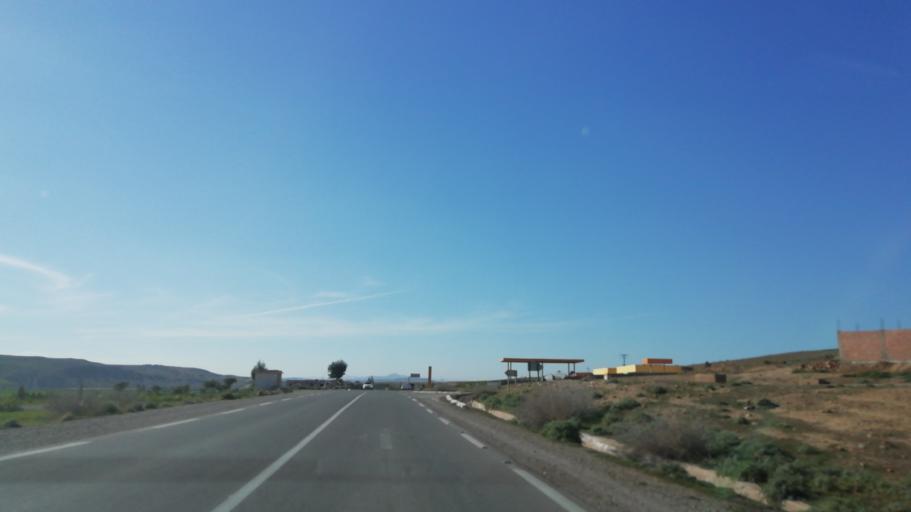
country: DZ
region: Mascara
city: Oued el Abtal
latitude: 35.4507
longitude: 0.7828
